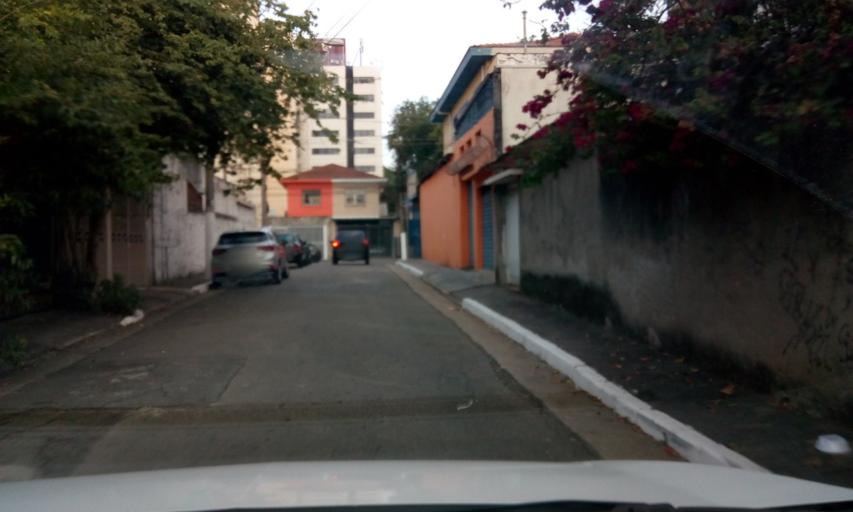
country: BR
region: Sao Paulo
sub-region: Diadema
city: Diadema
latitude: -23.6275
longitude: -46.6464
